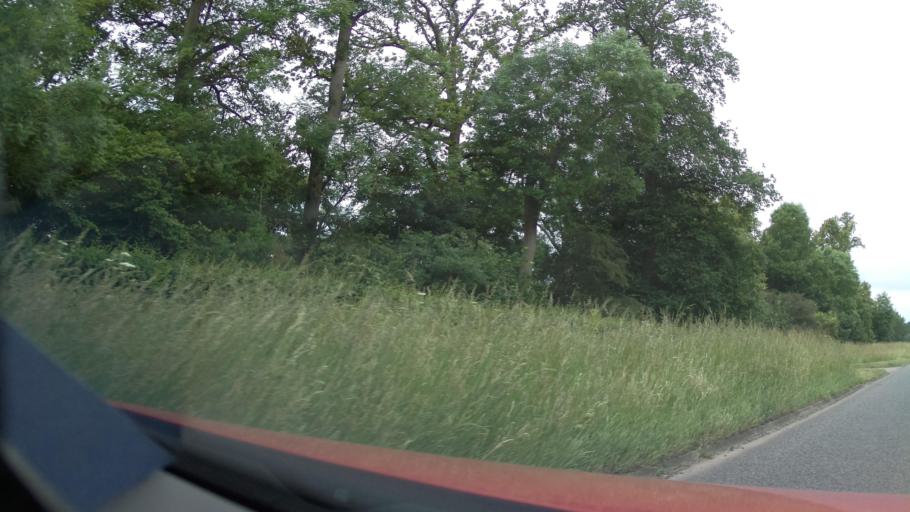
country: GB
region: England
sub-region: District of Rutland
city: Burley
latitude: 52.6742
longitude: -0.6795
